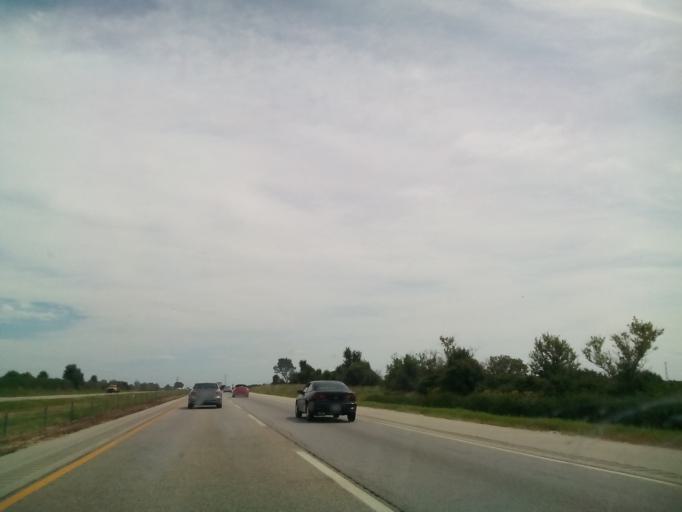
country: US
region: Illinois
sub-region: Kane County
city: Sugar Grove
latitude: 41.8148
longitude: -88.4532
